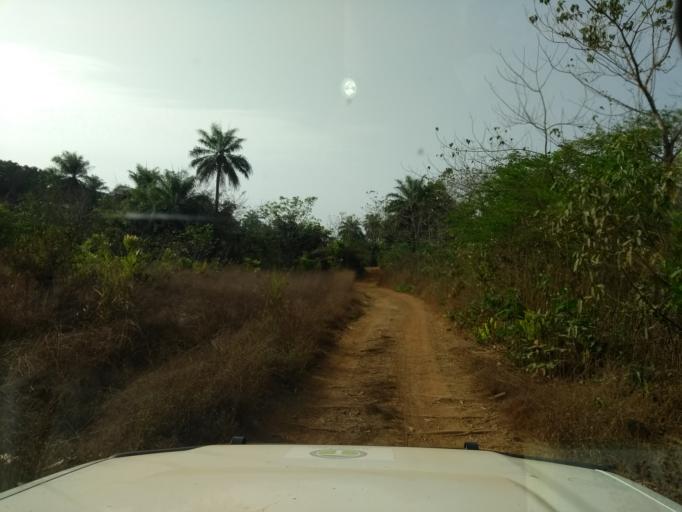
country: GN
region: Kindia
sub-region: Prefecture de Dubreka
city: Dubreka
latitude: 9.8396
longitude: -13.5603
